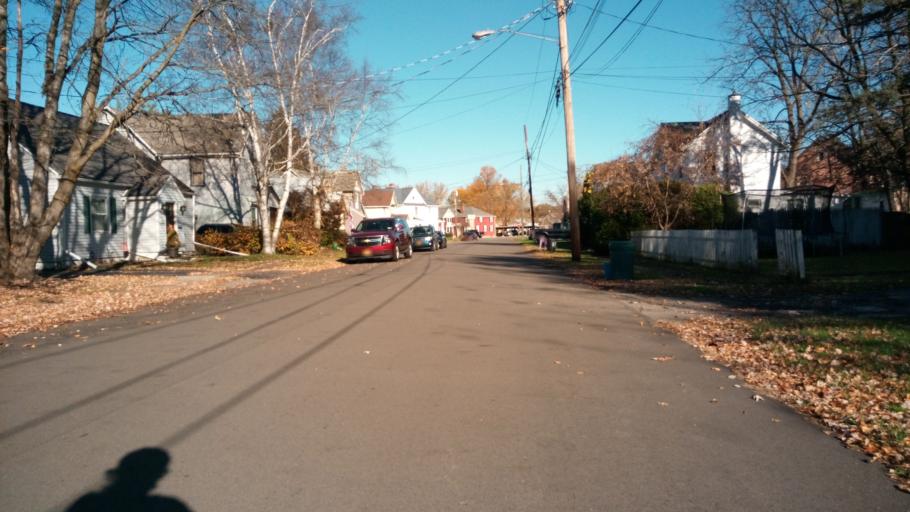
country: US
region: New York
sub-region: Chemung County
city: Southport
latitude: 42.0653
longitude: -76.8093
